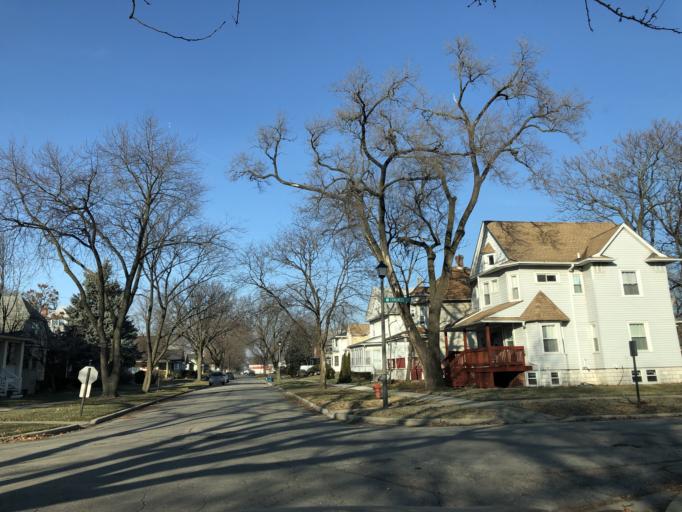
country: US
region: Illinois
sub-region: Cook County
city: Maywood
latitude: 41.8725
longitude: -87.8373
